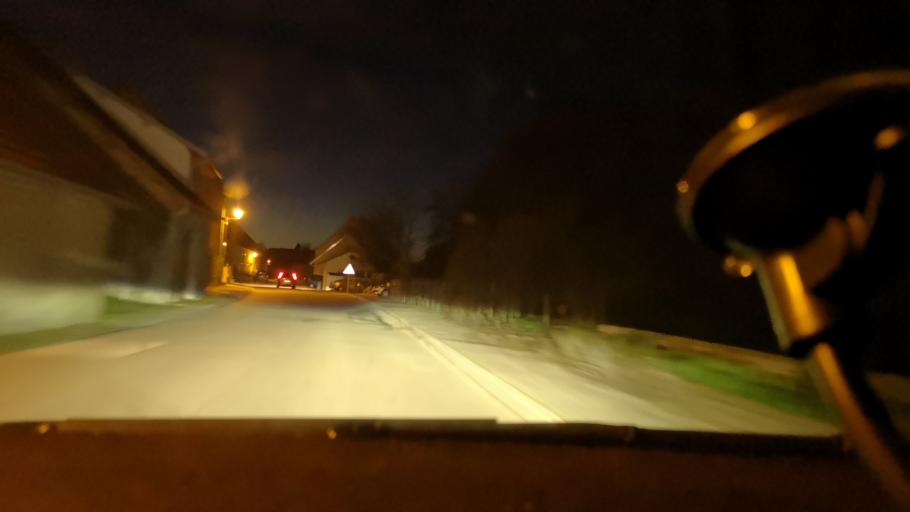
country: FR
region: Franche-Comte
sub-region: Departement du Jura
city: Bletterans
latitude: 46.7607
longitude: 5.5259
